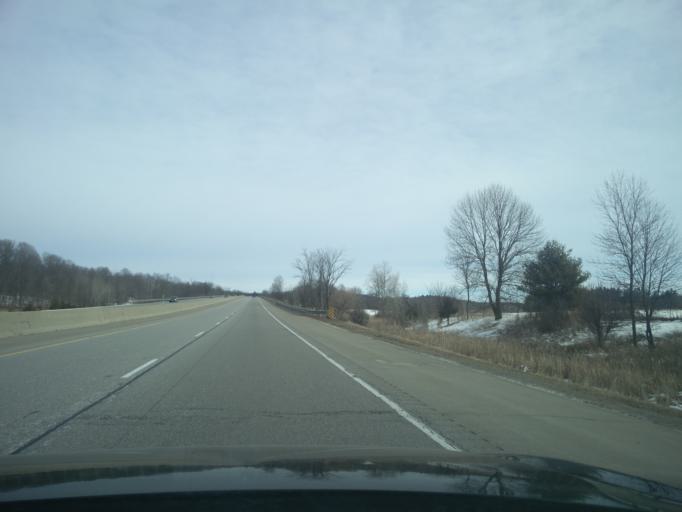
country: CA
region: Ontario
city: Brockville
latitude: 44.5725
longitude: -75.7372
